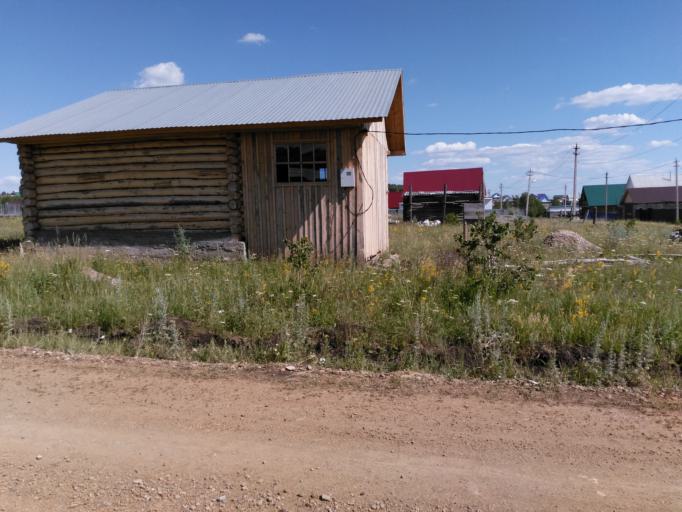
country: RU
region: Bashkortostan
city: Uchaly
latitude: 54.2893
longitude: 59.3618
